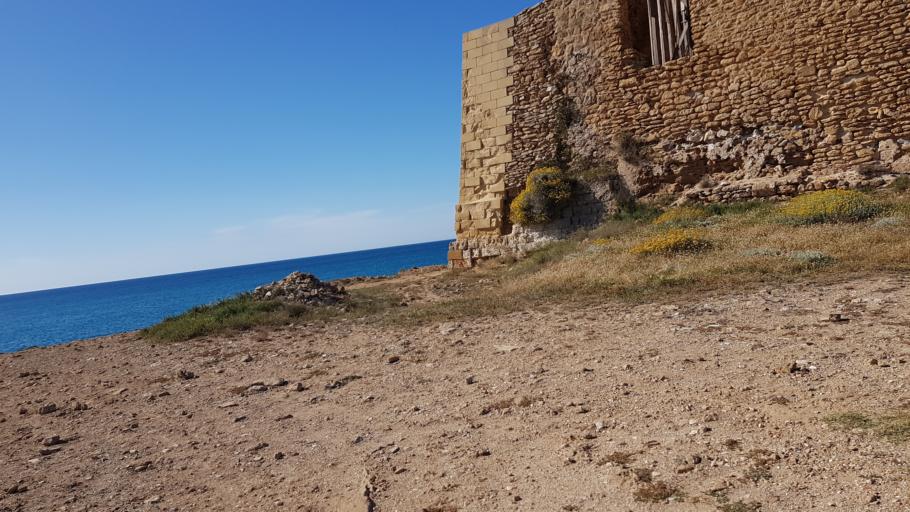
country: IT
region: Apulia
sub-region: Provincia di Brindisi
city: Brindisi
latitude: 40.6881
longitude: 17.8696
